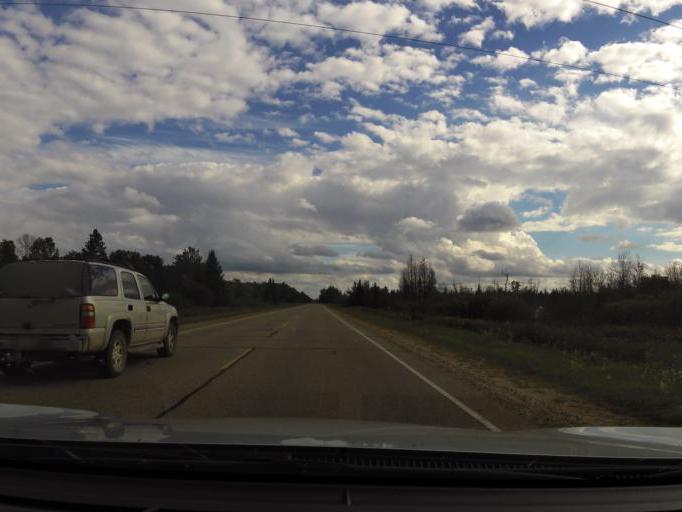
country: US
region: Michigan
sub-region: Roscommon County
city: Roscommon
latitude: 44.4504
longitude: -84.5212
